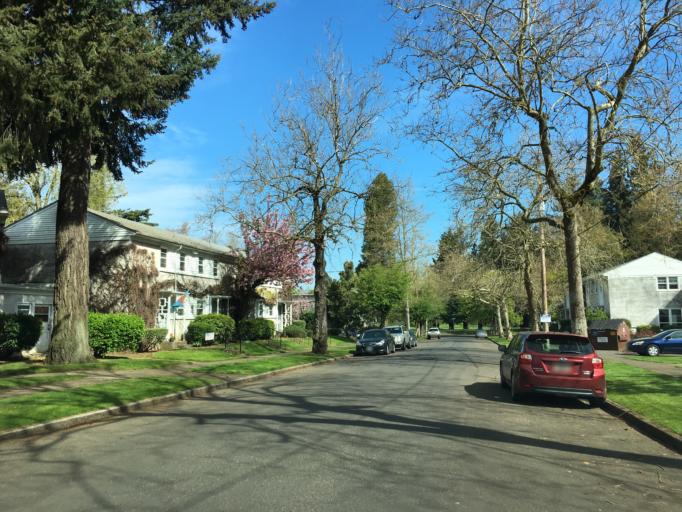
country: US
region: Oregon
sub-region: Multnomah County
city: Lents
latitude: 45.5361
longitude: -122.5912
